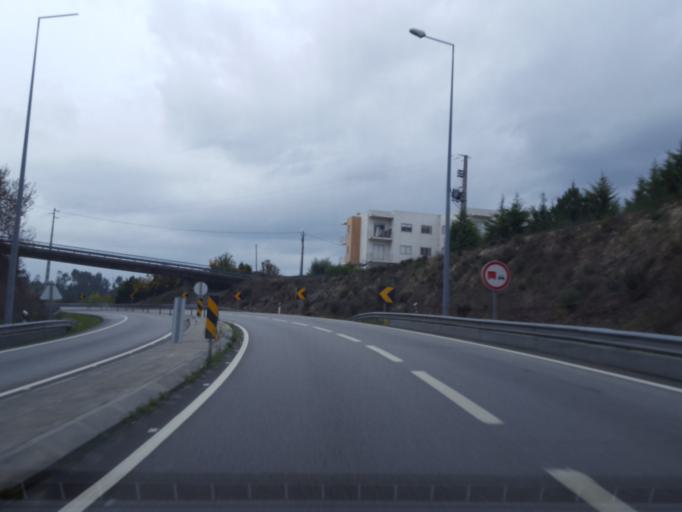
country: PT
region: Porto
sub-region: Marco de Canaveses
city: Marco de Canavezes
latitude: 41.2102
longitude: -8.1656
